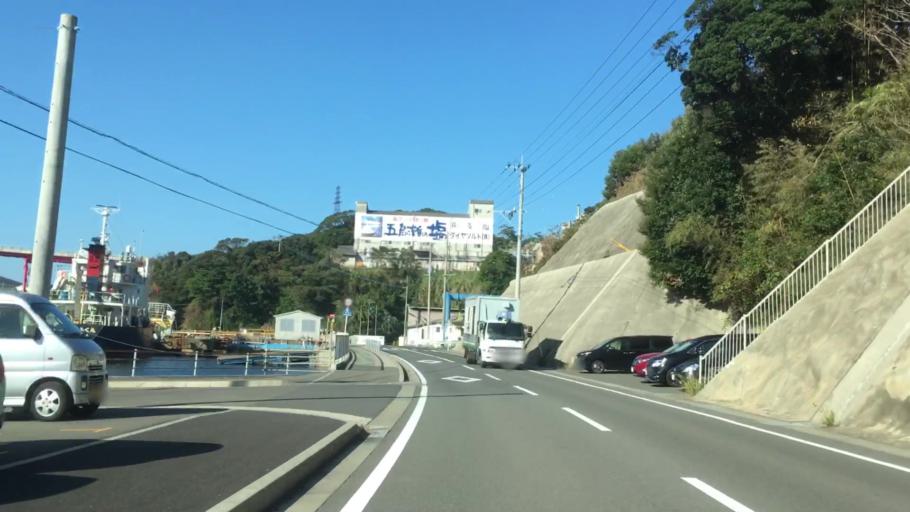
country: JP
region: Nagasaki
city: Sasebo
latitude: 33.0242
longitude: 129.5741
